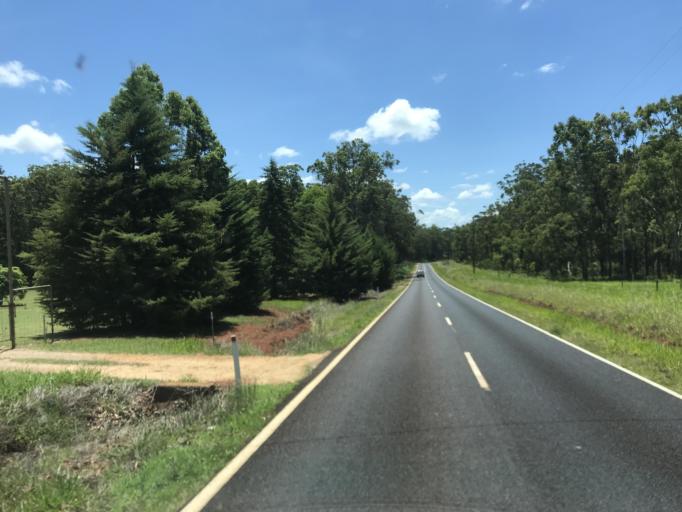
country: AU
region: Queensland
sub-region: Tablelands
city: Atherton
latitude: -17.4300
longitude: 145.4044
